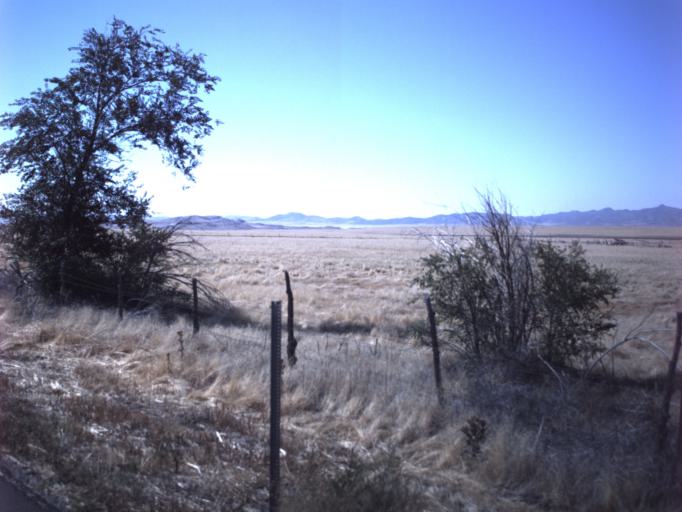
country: US
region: Utah
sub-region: Tooele County
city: Grantsville
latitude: 40.4327
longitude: -112.7487
